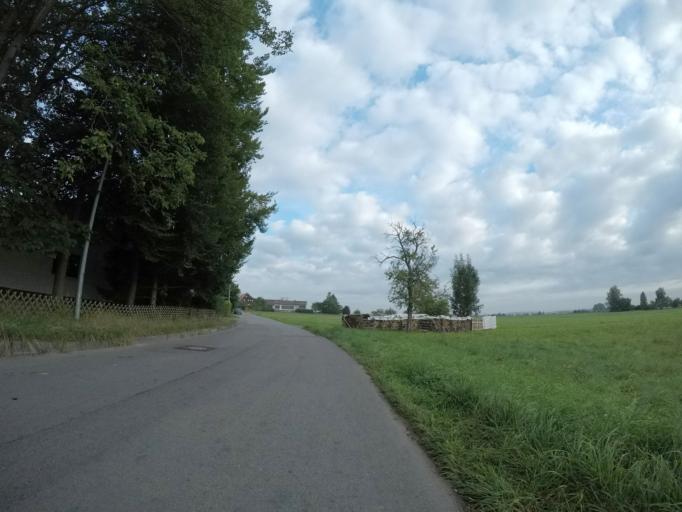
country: DE
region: Baden-Wuerttemberg
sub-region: Tuebingen Region
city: Sickenhausen
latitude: 48.5197
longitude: 9.1813
